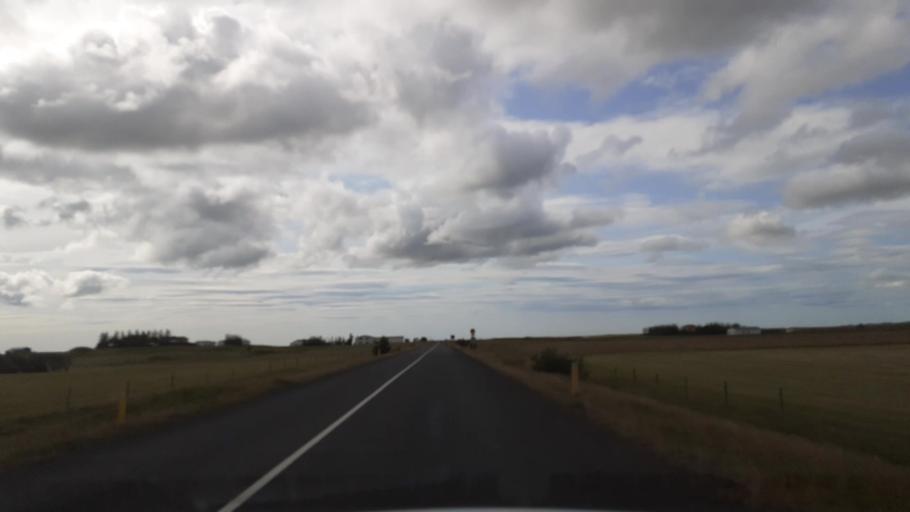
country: IS
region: South
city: Vestmannaeyjar
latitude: 63.8405
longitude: -20.4096
